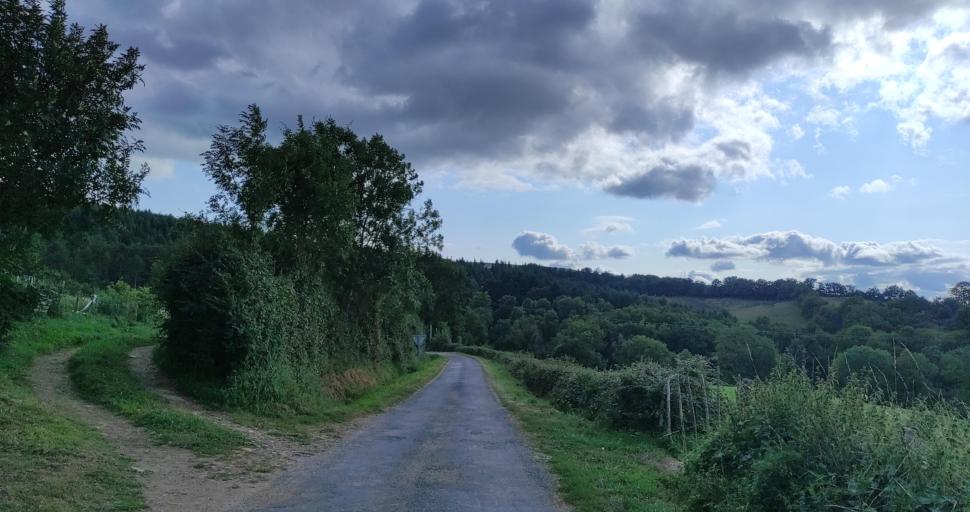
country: FR
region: Midi-Pyrenees
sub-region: Departement de l'Aveyron
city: La Loubiere
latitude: 44.3826
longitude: 2.7091
